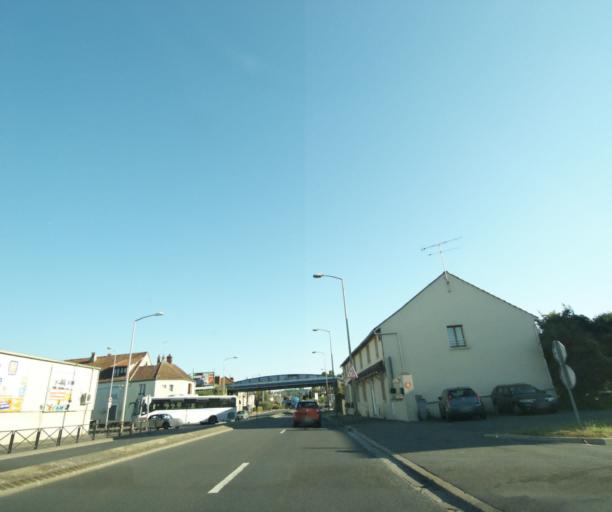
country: FR
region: Ile-de-France
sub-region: Departement de Seine-et-Marne
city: Montereau-Fault-Yonne
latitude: 48.3766
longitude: 2.9569
